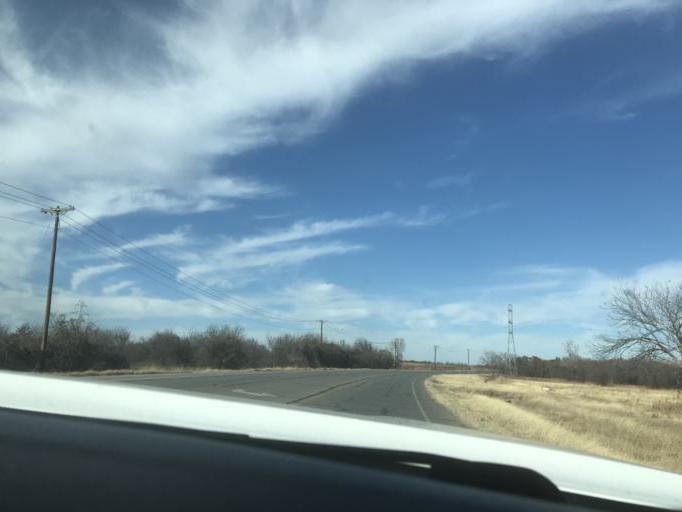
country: US
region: Texas
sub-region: Erath County
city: Stephenville
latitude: 32.2063
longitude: -98.2478
